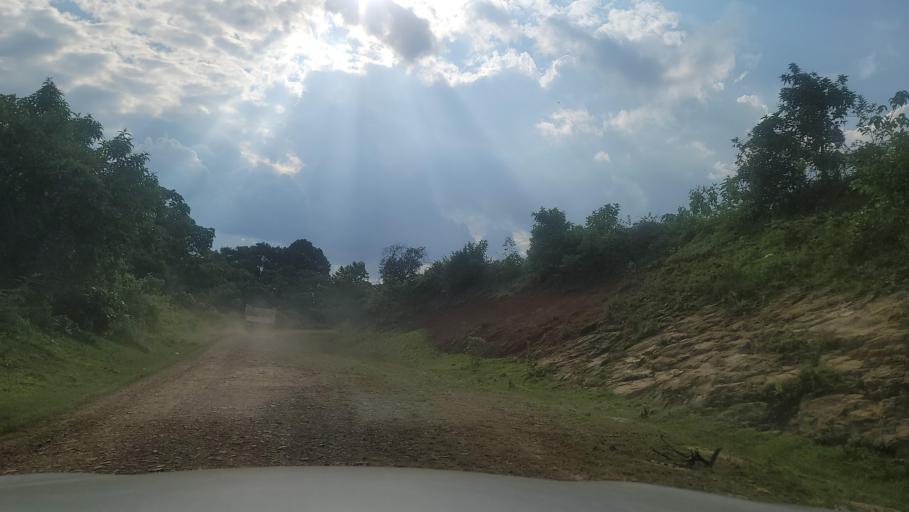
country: ET
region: Southern Nations, Nationalities, and People's Region
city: Bonga
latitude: 7.5786
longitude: 36.1591
